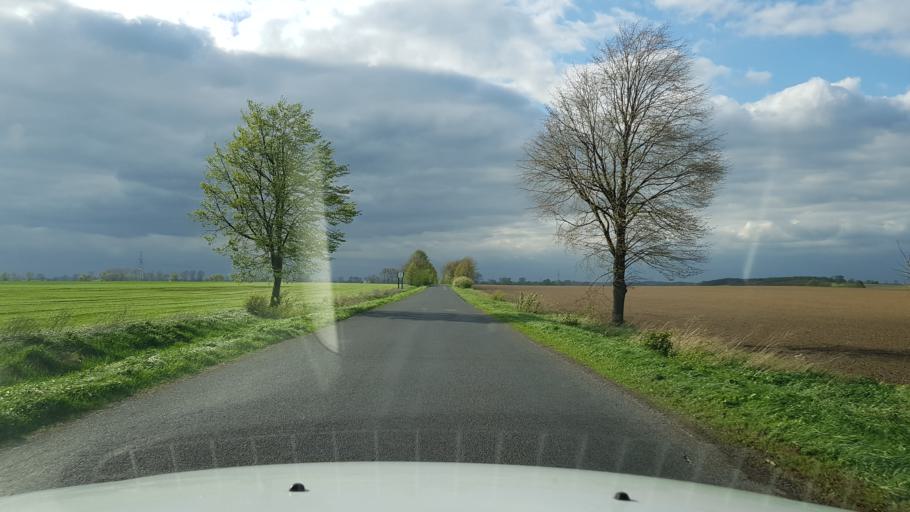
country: PL
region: West Pomeranian Voivodeship
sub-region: Powiat pyrzycki
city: Przelewice
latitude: 53.1298
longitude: 15.0475
